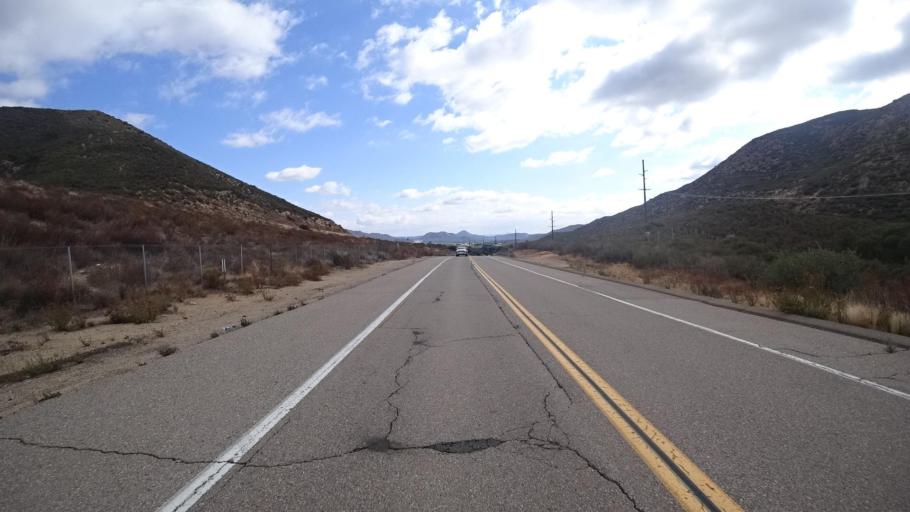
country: US
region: California
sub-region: San Diego County
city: Pine Valley
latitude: 32.7796
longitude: -116.4940
